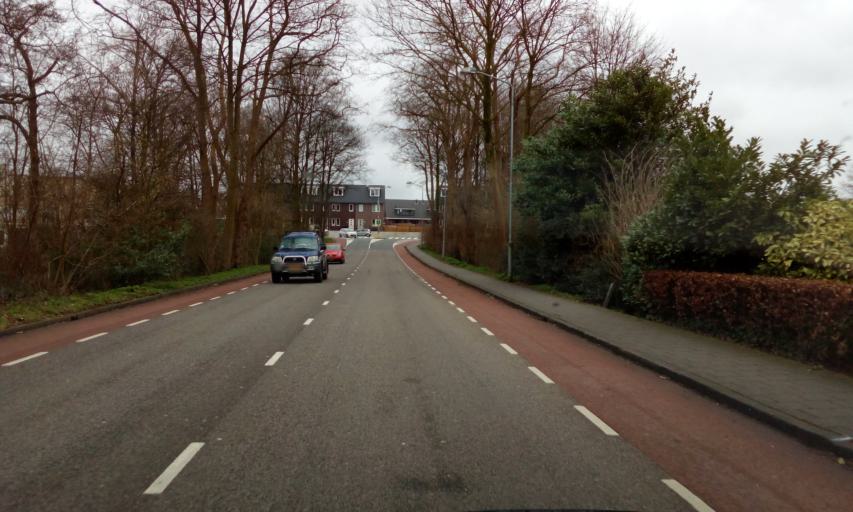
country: NL
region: South Holland
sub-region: Gemeente Alblasserdam
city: Alblasserdam
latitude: 51.8644
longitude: 4.6541
